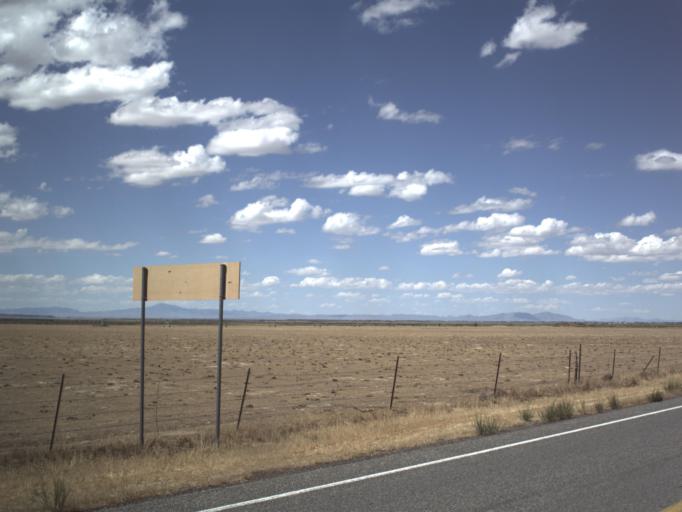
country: US
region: Utah
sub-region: Millard County
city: Delta
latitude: 39.2032
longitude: -112.4099
